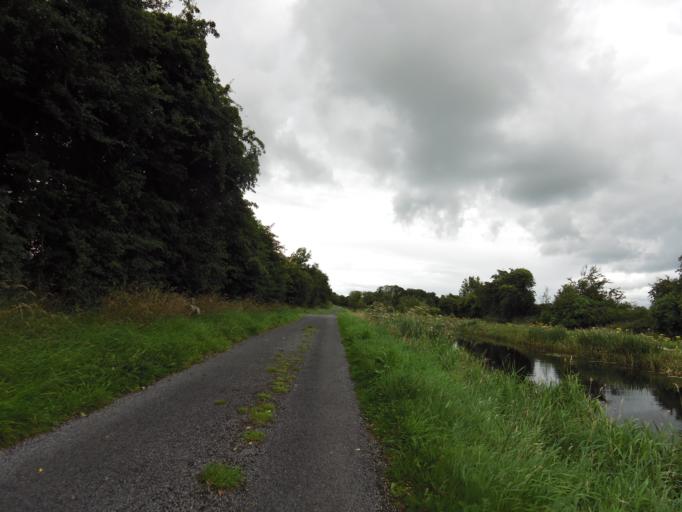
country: IE
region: Leinster
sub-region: An Iarmhi
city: An Muileann gCearr
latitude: 53.5420
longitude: -7.4746
